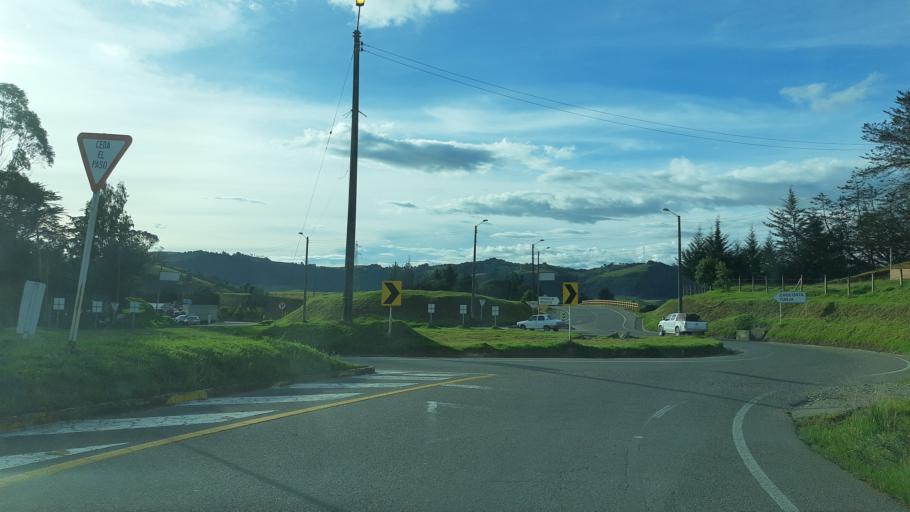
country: CO
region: Cundinamarca
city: Choconta
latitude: 5.0907
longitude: -73.7206
